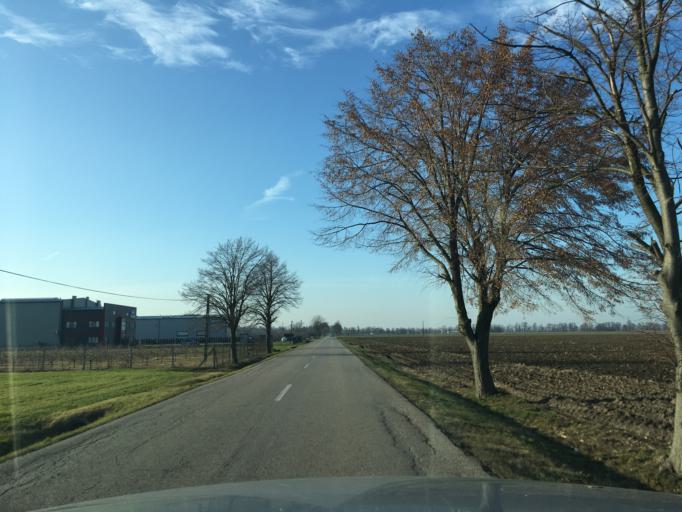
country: PL
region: Masovian Voivodeship
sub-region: Powiat pruszkowski
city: Nadarzyn
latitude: 52.0421
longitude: 20.8082
